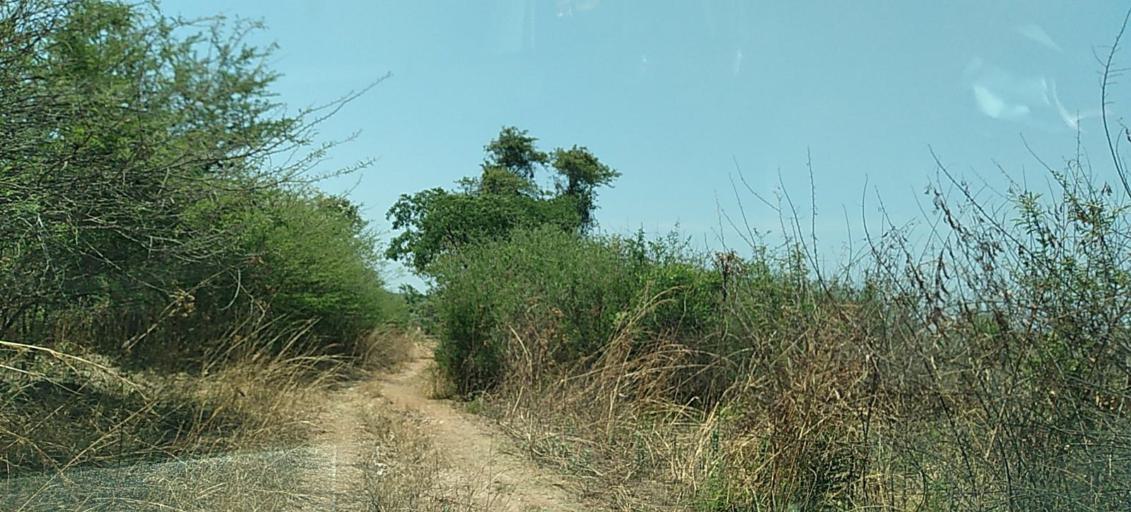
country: ZM
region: Copperbelt
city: Luanshya
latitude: -12.9901
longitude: 28.3256
